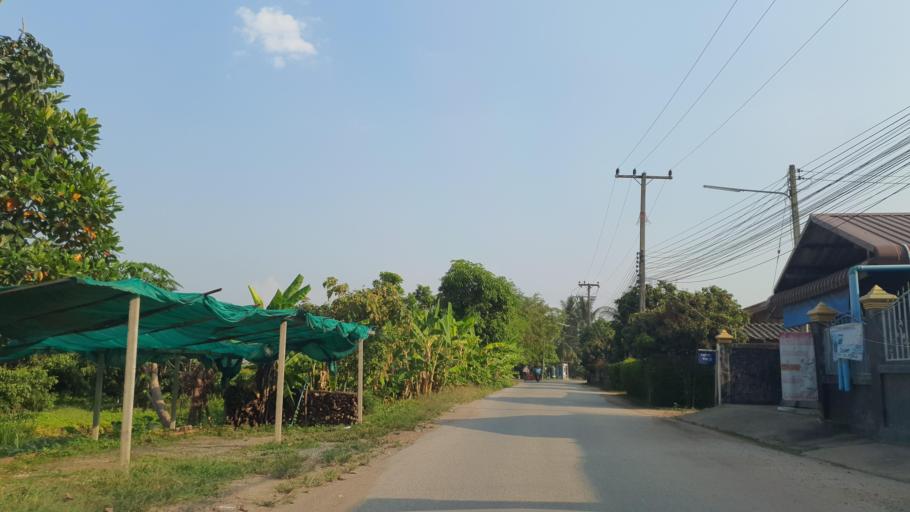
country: TH
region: Chiang Mai
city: Mae Wang
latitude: 18.6644
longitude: 98.8197
